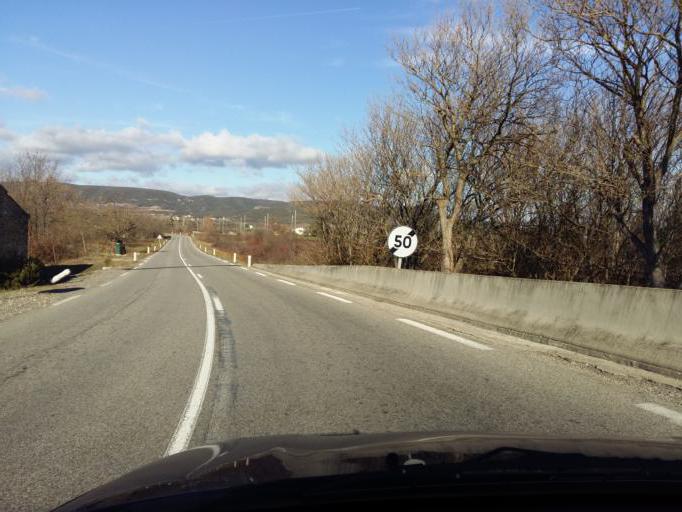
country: FR
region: Rhone-Alpes
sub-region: Departement de l'Ardeche
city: Bourg-Saint-Andeol
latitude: 44.4156
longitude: 4.6540
